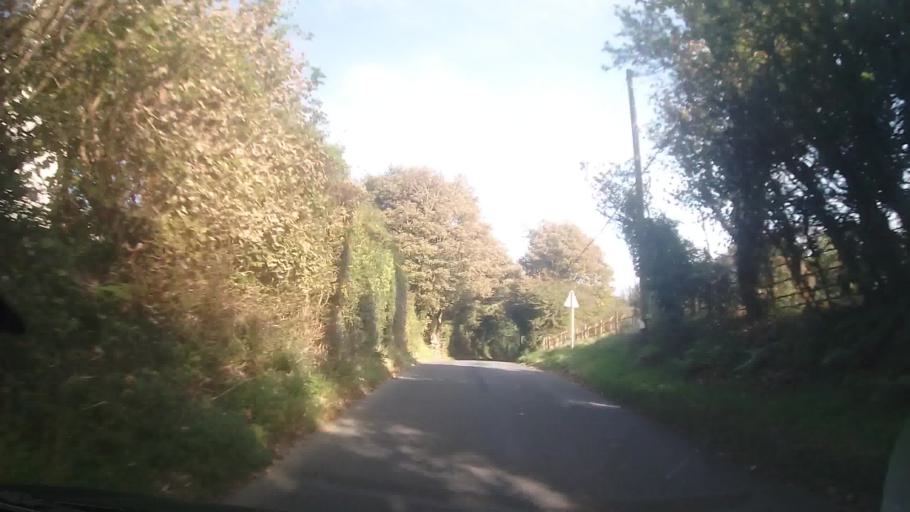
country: GB
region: Wales
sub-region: Pembrokeshire
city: Fishguard
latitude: 51.9840
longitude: -4.9518
